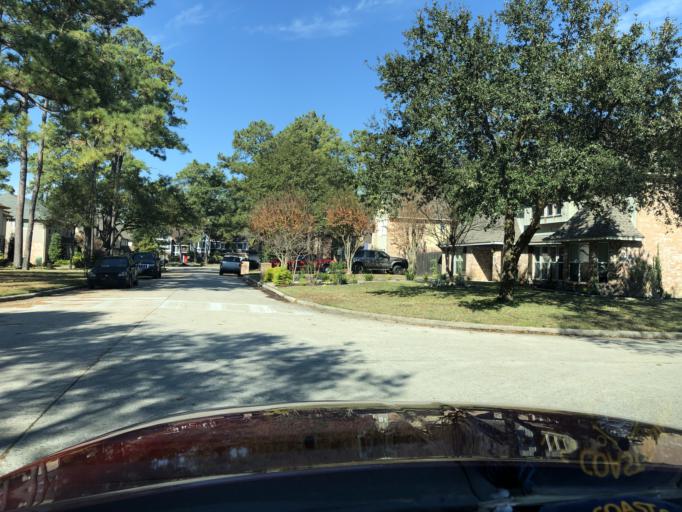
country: US
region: Texas
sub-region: Harris County
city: Tomball
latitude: 30.0238
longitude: -95.5508
